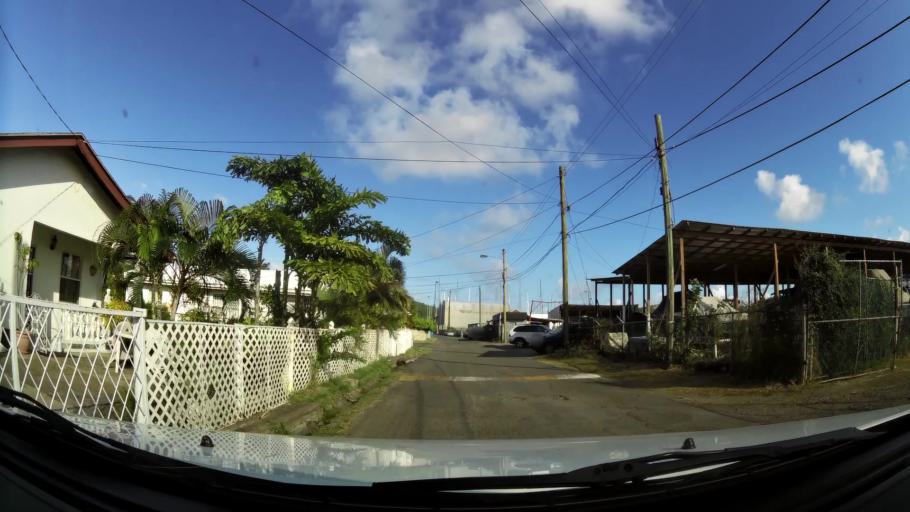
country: LC
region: Gros-Islet
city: Gros Islet
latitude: 14.0789
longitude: -60.9513
